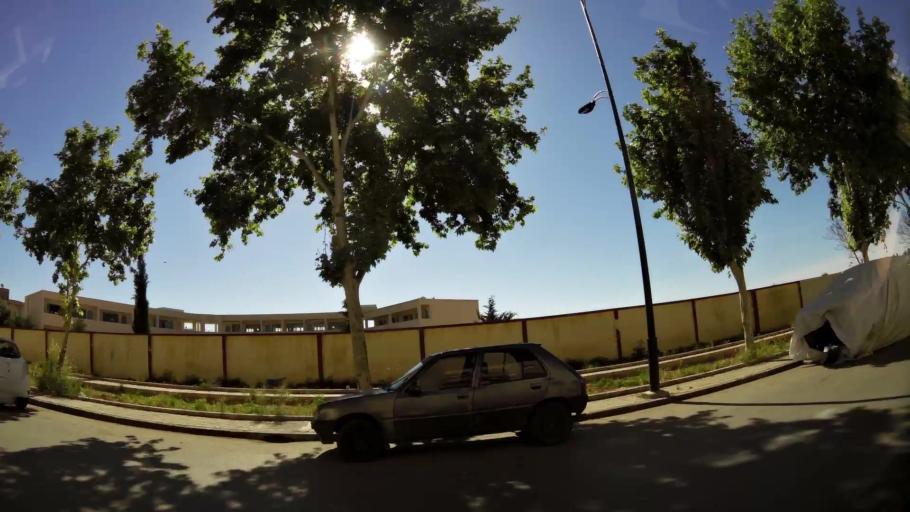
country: MA
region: Fes-Boulemane
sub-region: Fes
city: Fes
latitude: 34.0198
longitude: -4.9814
